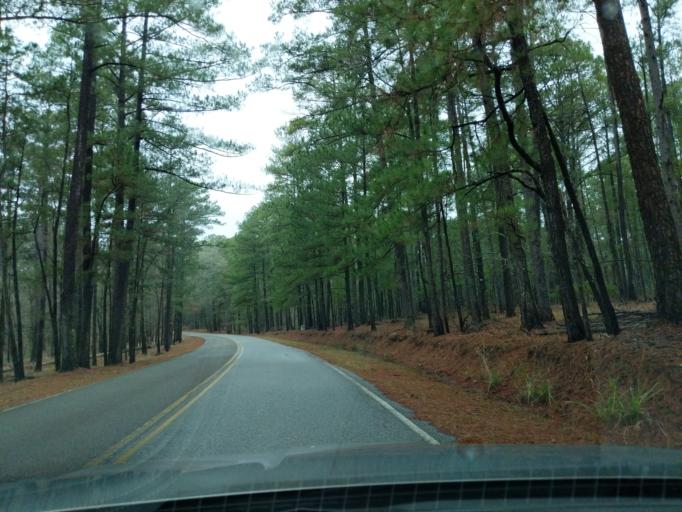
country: US
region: Georgia
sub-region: Columbia County
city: Appling
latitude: 33.6479
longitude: -82.3794
